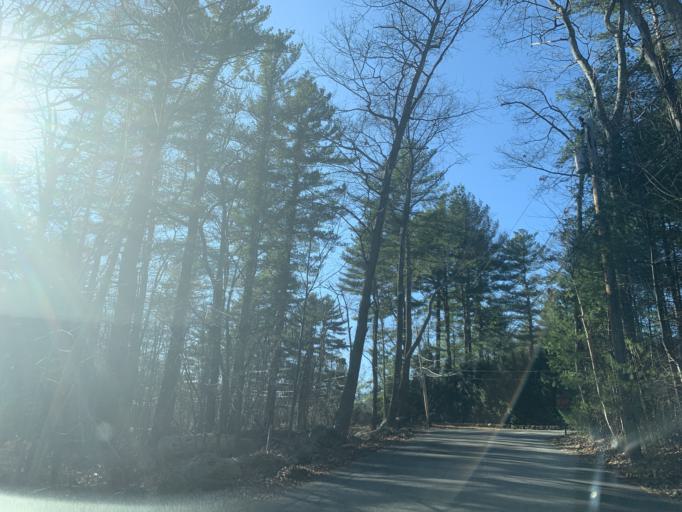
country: US
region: Massachusetts
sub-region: Middlesex County
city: Weston
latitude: 42.3757
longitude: -71.2992
